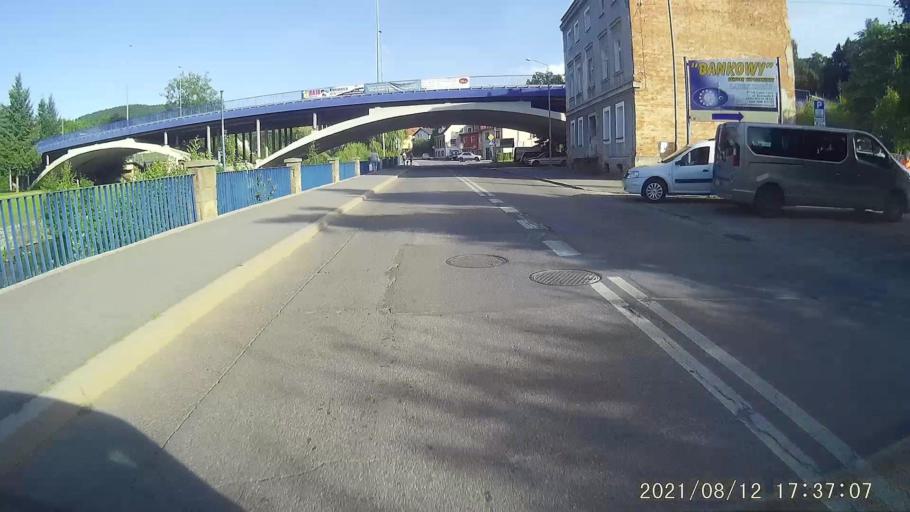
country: PL
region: Lower Silesian Voivodeship
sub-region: Powiat klodzki
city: Ladek-Zdroj
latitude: 50.3441
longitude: 16.8787
